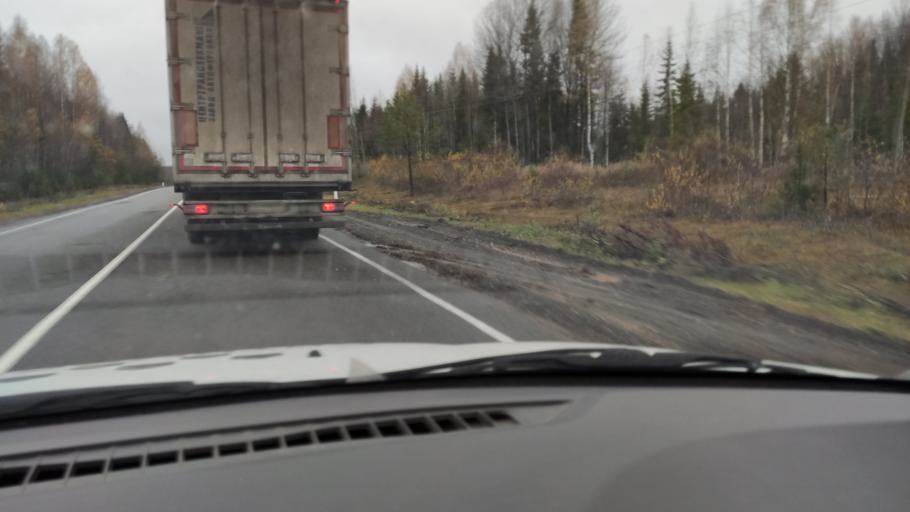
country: RU
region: Kirov
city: Omutninsk
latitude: 58.7523
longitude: 52.0514
